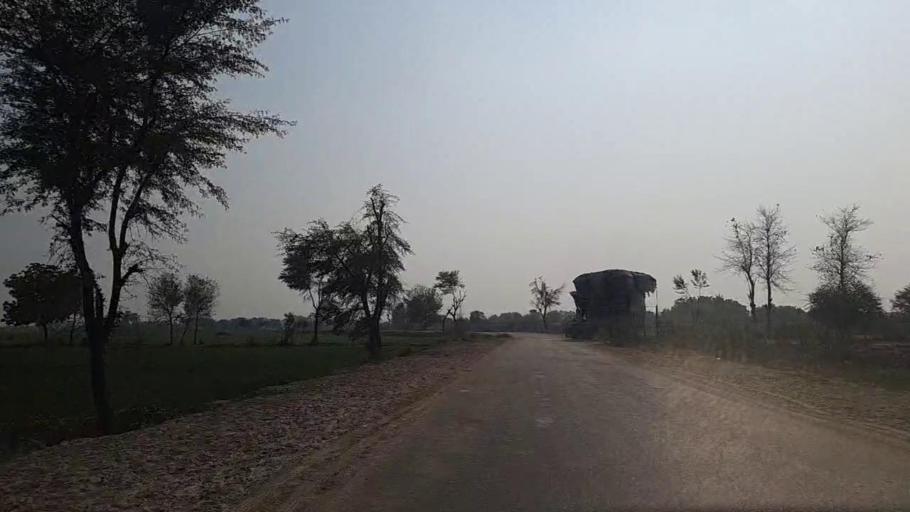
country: PK
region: Sindh
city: Jam Sahib
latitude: 26.3406
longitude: 68.5341
